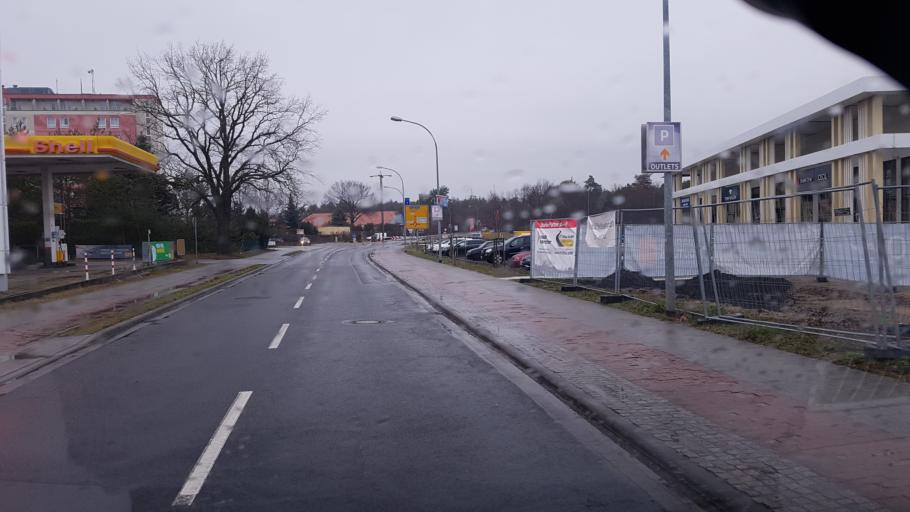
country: DE
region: Brandenburg
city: Ruhland
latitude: 51.4703
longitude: 13.8692
